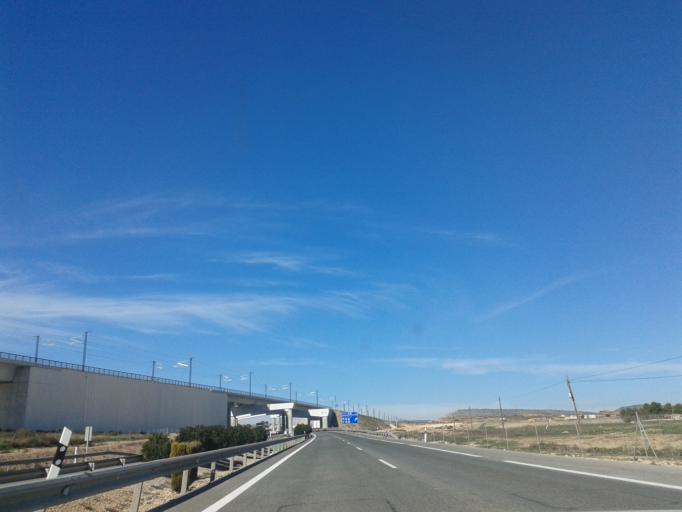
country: ES
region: Castille-La Mancha
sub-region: Provincia de Albacete
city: Caudete
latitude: 38.7186
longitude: -0.9311
